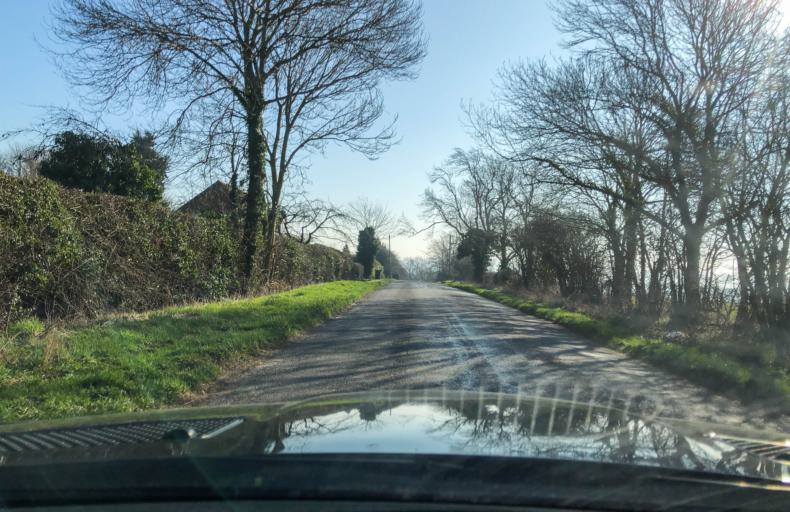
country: GB
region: England
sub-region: Warwickshire
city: Wellesbourne Mountford
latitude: 52.1669
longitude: -1.5203
